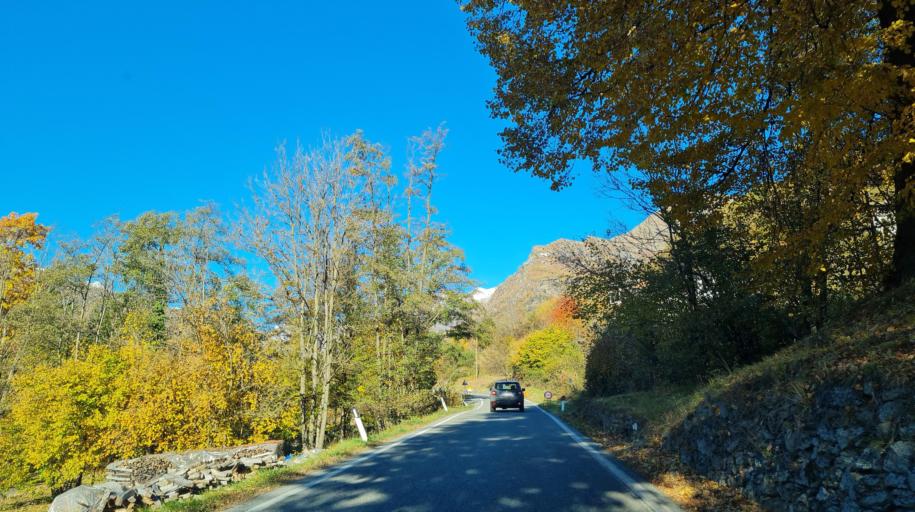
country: IT
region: Piedmont
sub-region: Provincia di Torino
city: Traversella
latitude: 45.5008
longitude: 7.7577
